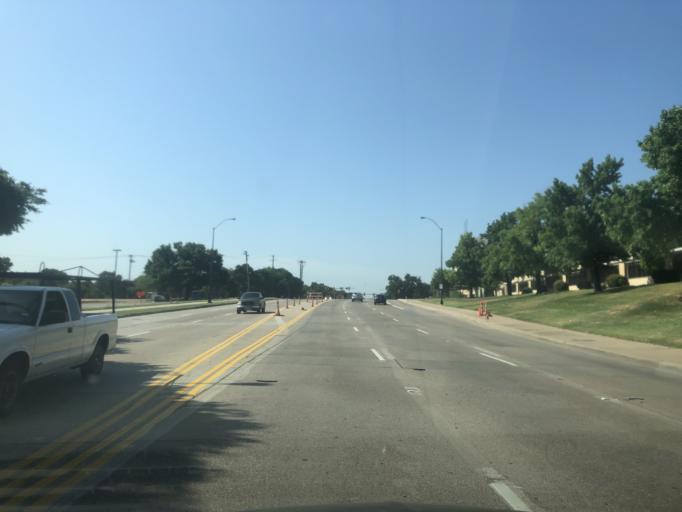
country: US
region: Texas
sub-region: Tarrant County
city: Fort Worth
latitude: 32.7452
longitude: -97.3616
